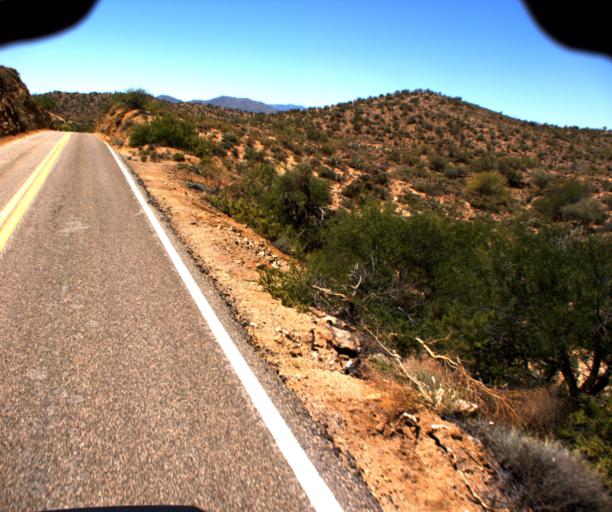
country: US
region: Arizona
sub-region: Yavapai County
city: Bagdad
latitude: 34.4534
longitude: -112.9883
